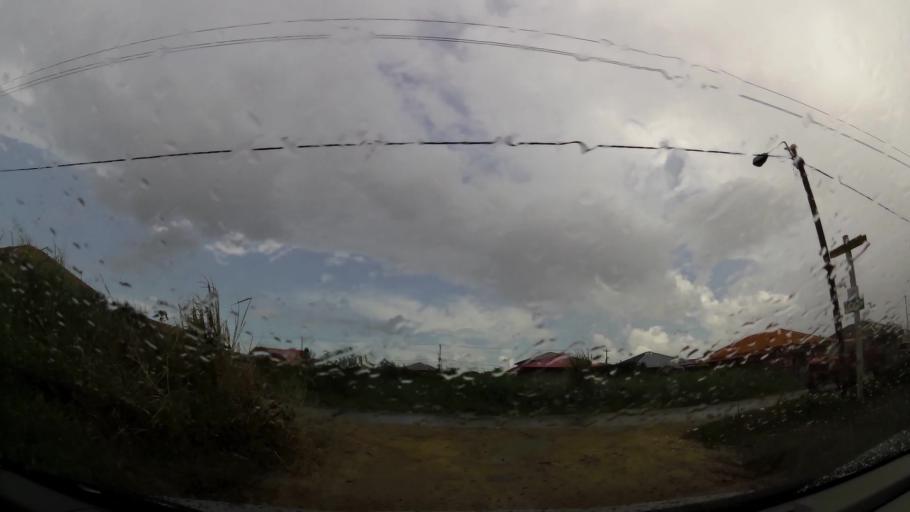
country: SR
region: Commewijne
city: Nieuw Amsterdam
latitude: 5.8529
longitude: -55.1168
